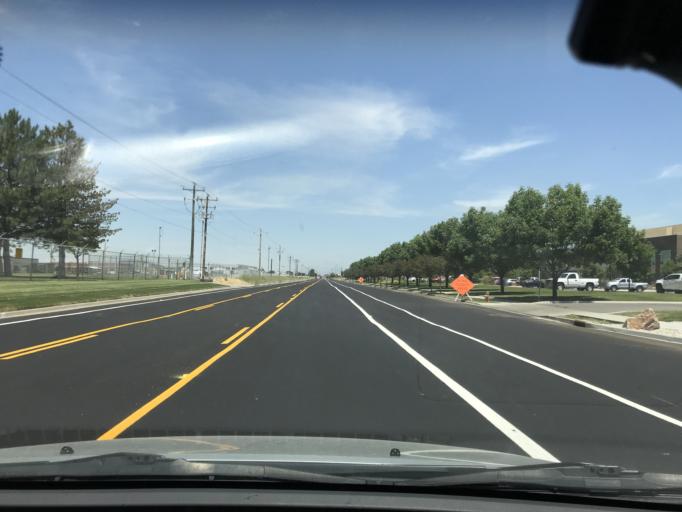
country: US
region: Utah
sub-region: Salt Lake County
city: Salt Lake City
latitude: 40.7888
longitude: -111.9536
